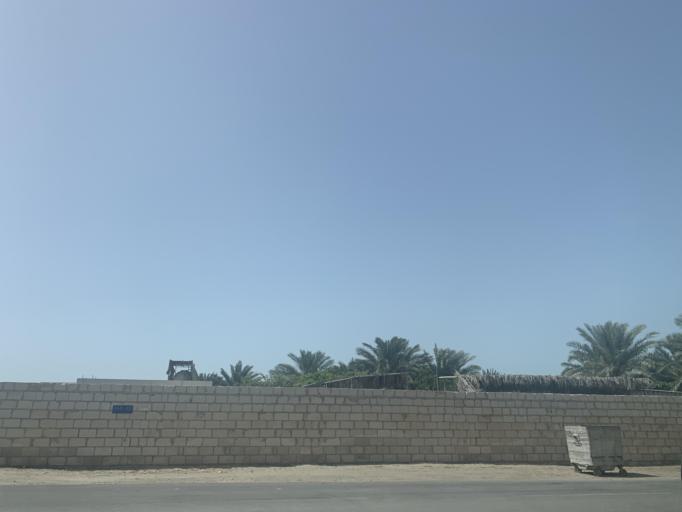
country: BH
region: Northern
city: Sitrah
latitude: 26.1702
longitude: 50.6140
